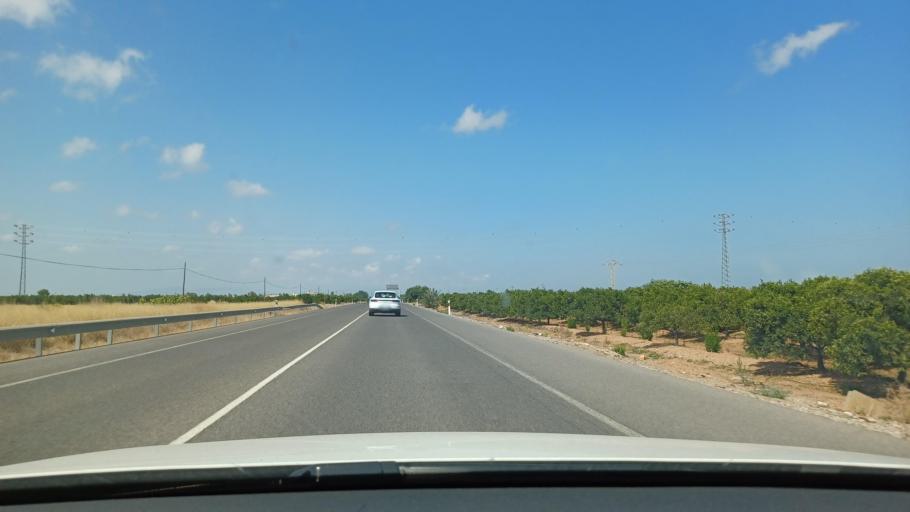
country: ES
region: Valencia
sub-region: Provincia de Castello
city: Moncofar
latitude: 39.8058
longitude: -0.1730
